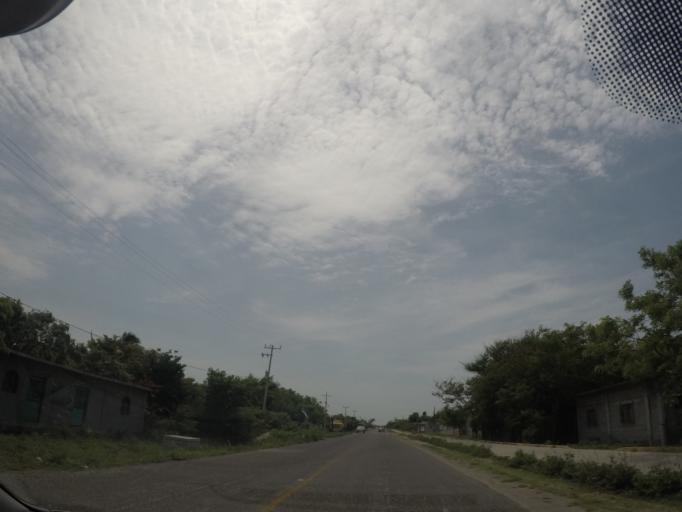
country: MX
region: Oaxaca
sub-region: San Mateo del Mar
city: Colonia Juarez
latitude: 16.2090
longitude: -95.0330
